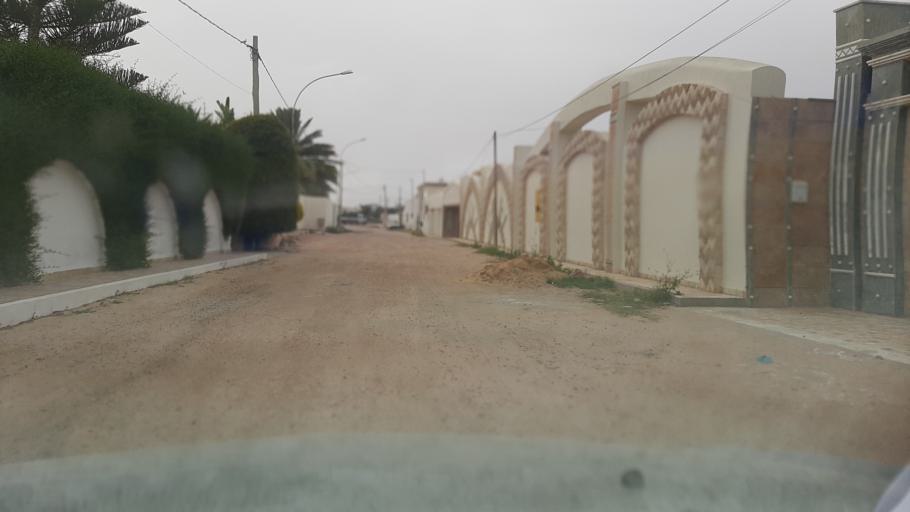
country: TN
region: Safaqis
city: Al Qarmadah
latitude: 34.7914
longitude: 10.7645
